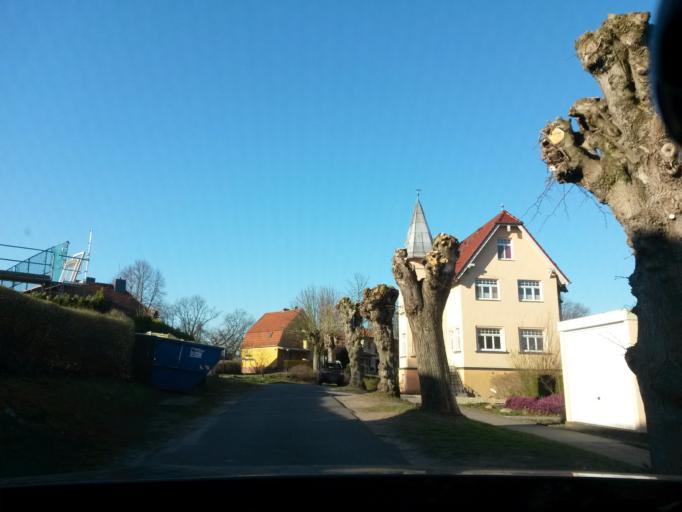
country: DE
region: Brandenburg
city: Buckow
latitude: 52.5705
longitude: 14.0671
